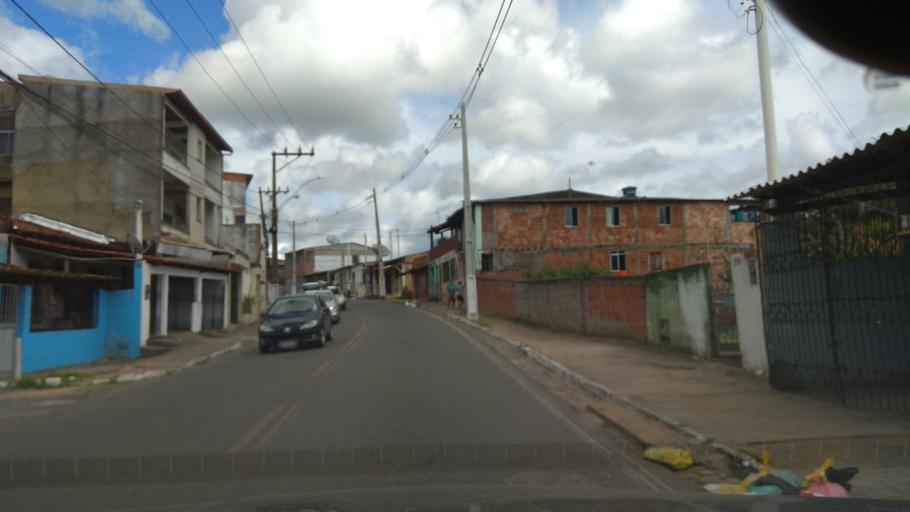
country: BR
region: Bahia
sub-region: Ilheus
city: Ilheus
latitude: -14.7845
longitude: -39.0589
